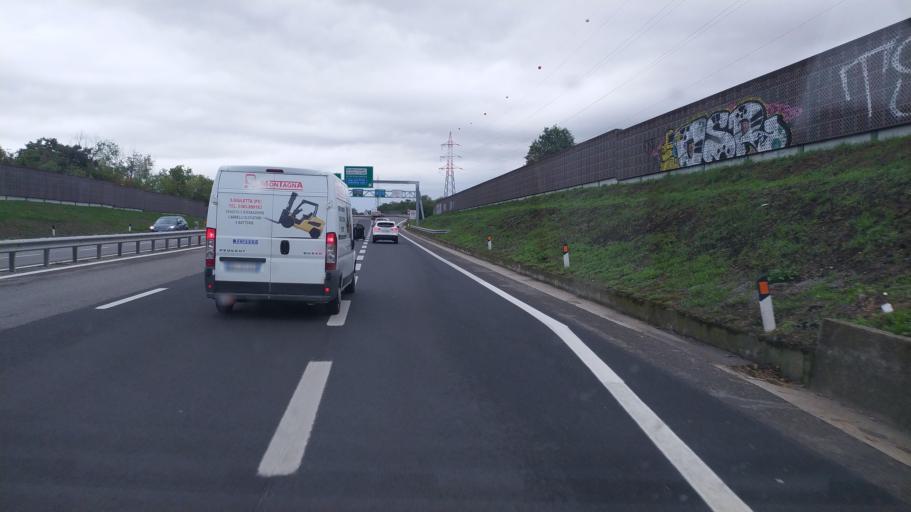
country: IT
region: Lombardy
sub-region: Provincia di Pavia
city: Pavia
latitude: 45.2029
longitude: 9.1441
